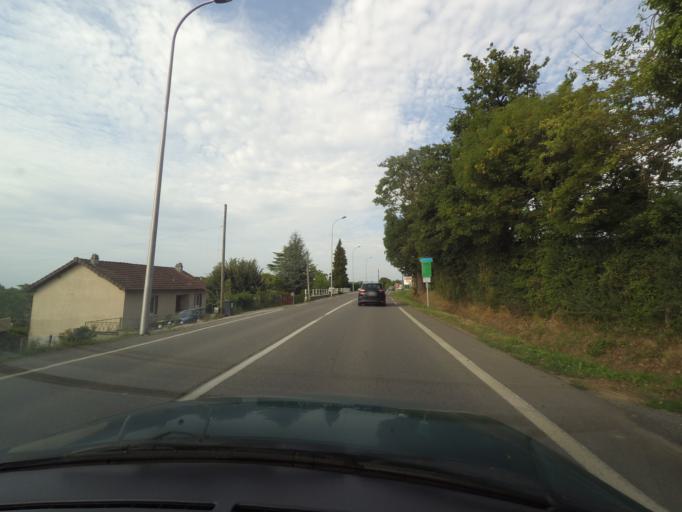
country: FR
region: Limousin
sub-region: Departement de la Haute-Vienne
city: Aixe-sur-Vienne
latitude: 45.7959
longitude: 1.1161
